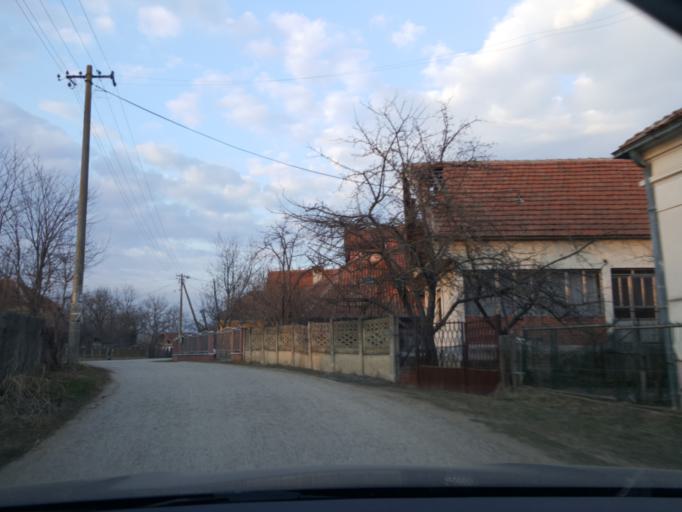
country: RS
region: Central Serbia
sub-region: Nisavski Okrug
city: Aleksinac
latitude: 43.5743
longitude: 21.6454
